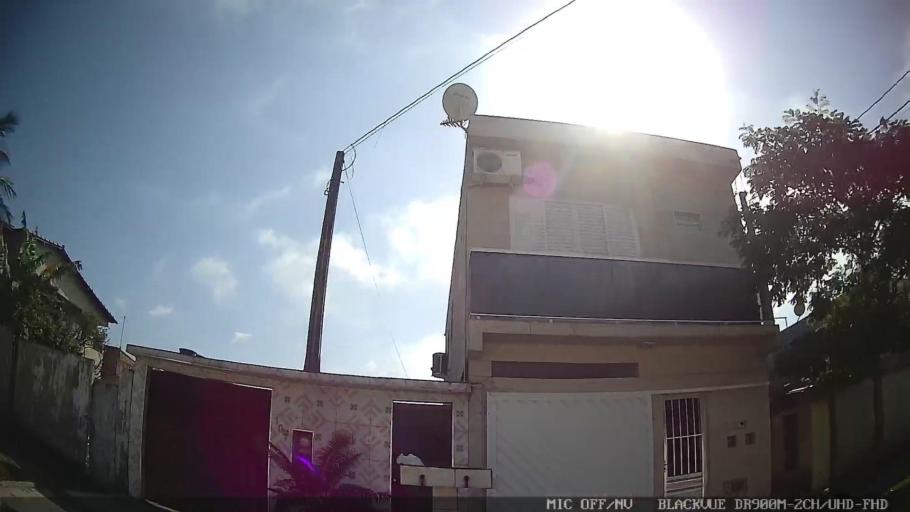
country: BR
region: Sao Paulo
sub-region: Guaruja
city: Guaruja
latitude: -23.9791
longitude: -46.1956
